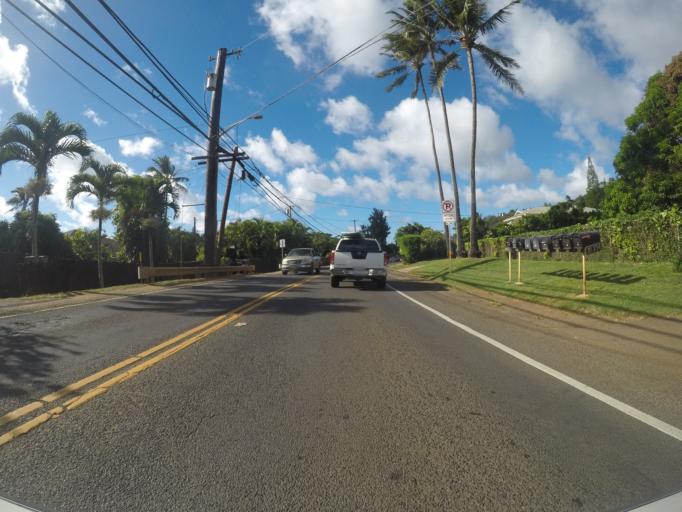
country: US
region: Hawaii
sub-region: Honolulu County
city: Pupukea
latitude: 21.6445
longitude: -158.0638
